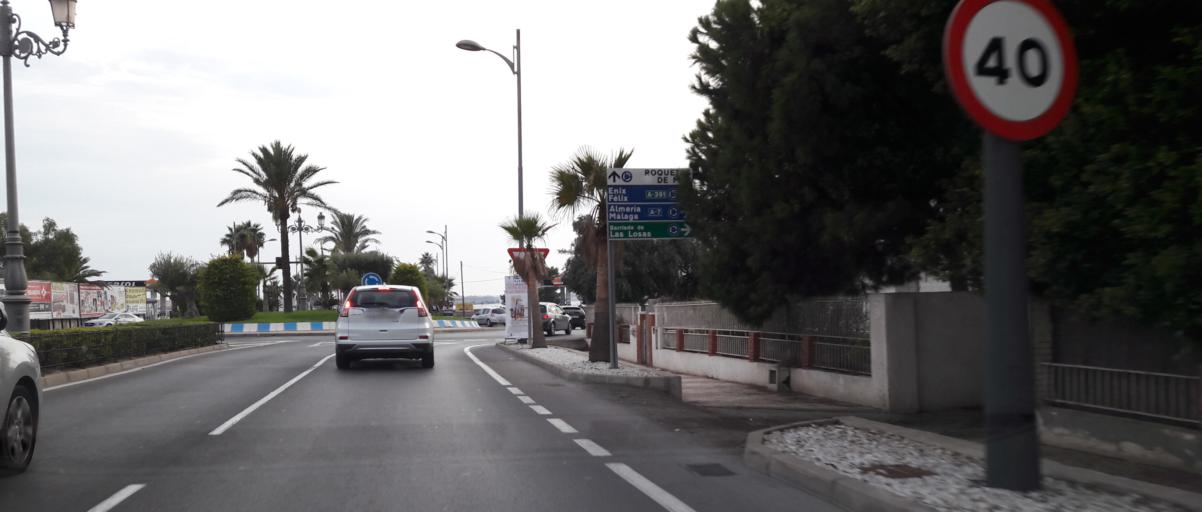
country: ES
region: Andalusia
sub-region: Provincia de Almeria
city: Aguadulce
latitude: 36.8002
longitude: -2.6012
